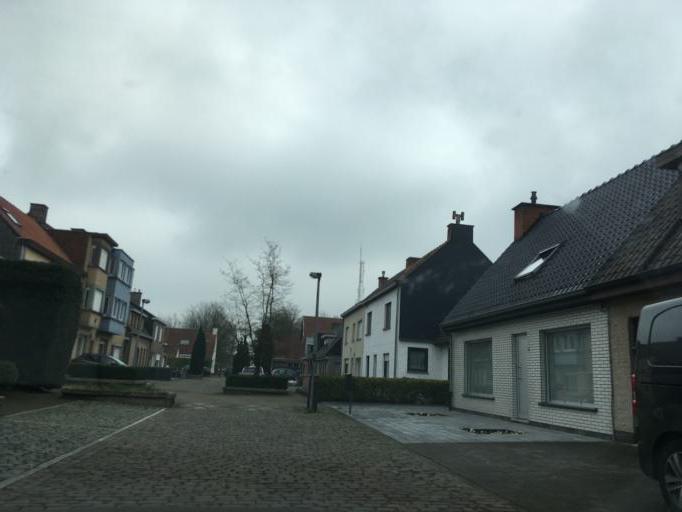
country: BE
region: Flanders
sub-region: Provincie West-Vlaanderen
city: Roeselare
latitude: 50.9359
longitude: 3.1171
